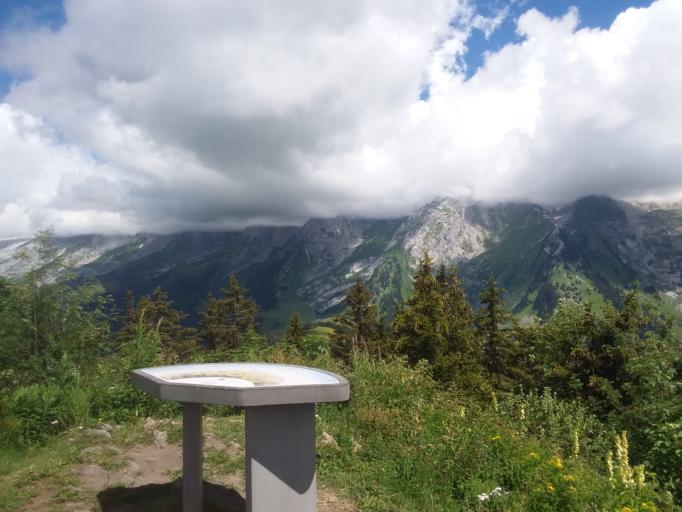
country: FR
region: Rhone-Alpes
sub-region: Departement de la Haute-Savoie
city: Le Grand-Bornand
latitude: 45.9221
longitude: 6.4483
